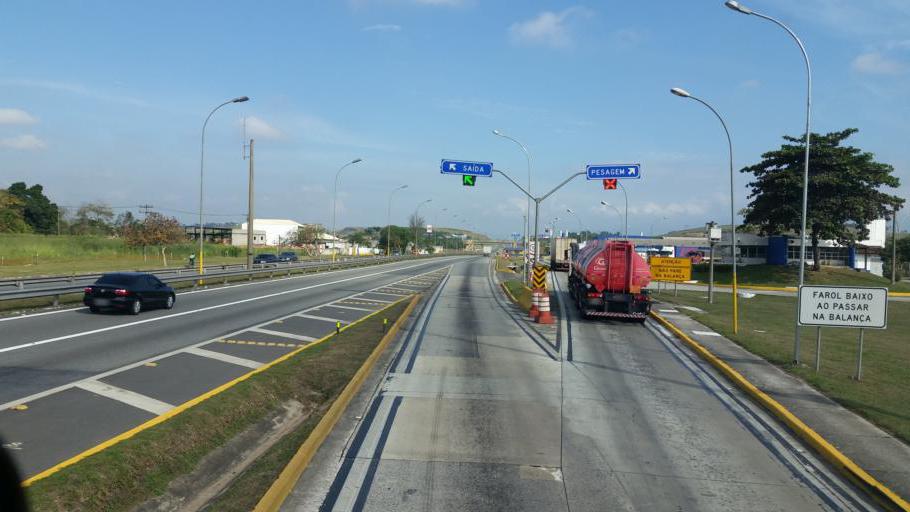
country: BR
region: Rio de Janeiro
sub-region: Resende
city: Resende
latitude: -22.4568
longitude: -44.4095
